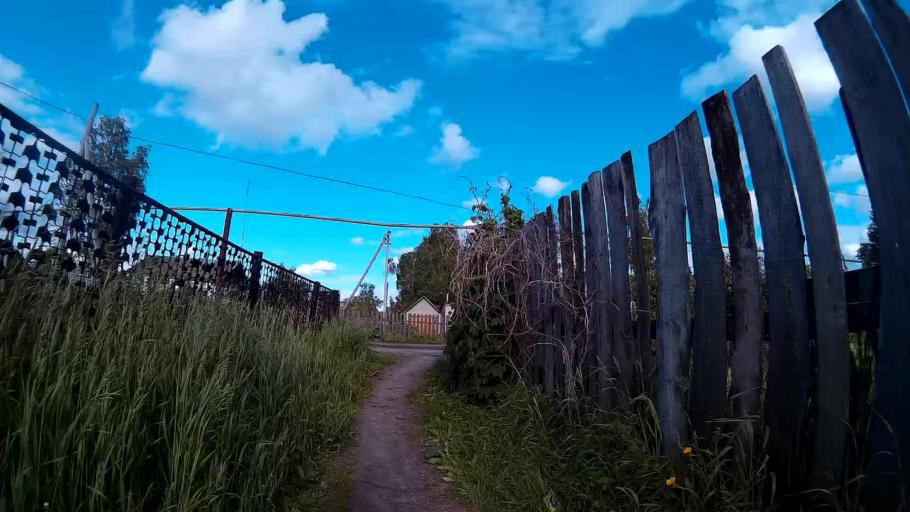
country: RU
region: Ulyanovsk
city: Novoul'yanovsk
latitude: 54.2055
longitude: 48.2658
